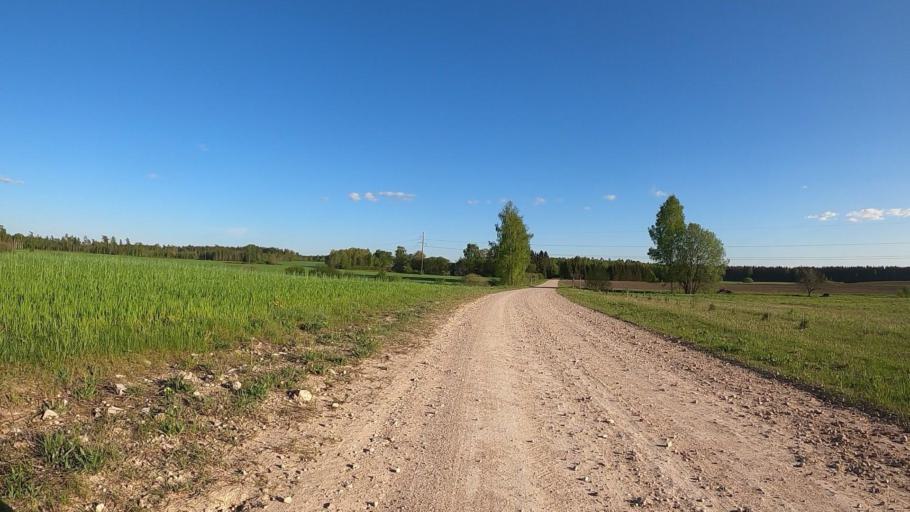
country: LV
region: Kekava
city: Kekava
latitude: 56.7708
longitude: 24.2876
